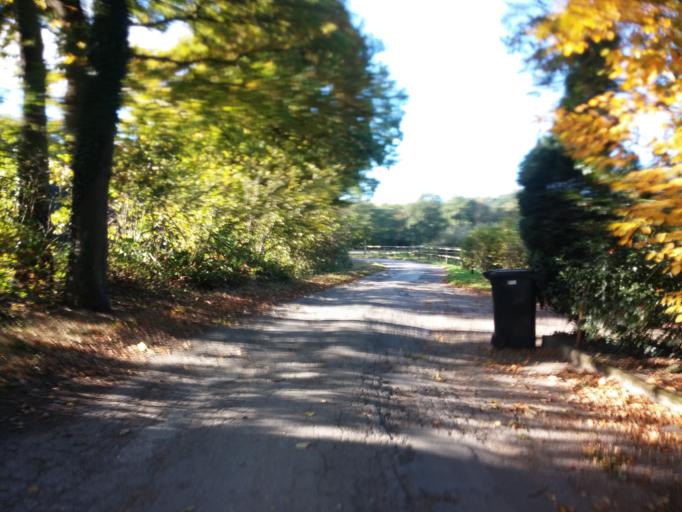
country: DE
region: North Rhine-Westphalia
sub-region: Regierungsbezirk Munster
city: Gladbeck
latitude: 51.6205
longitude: 6.9996
